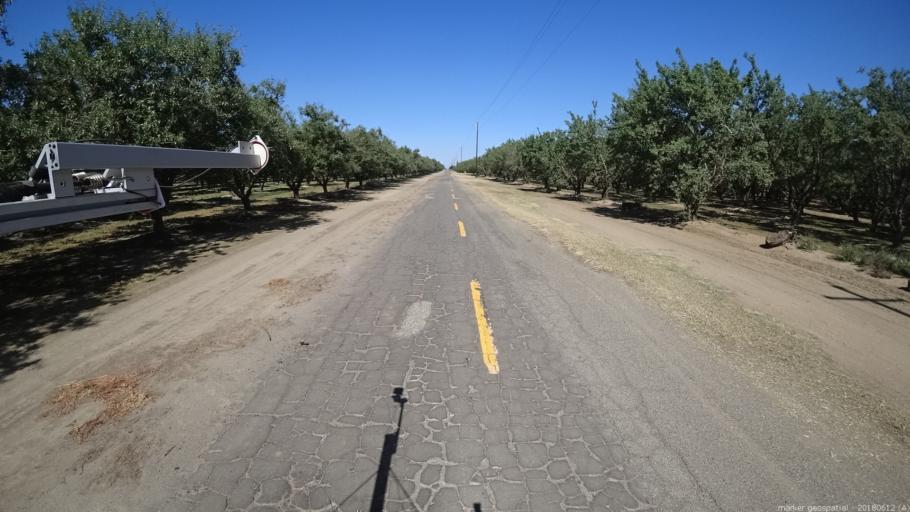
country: US
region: California
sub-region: Madera County
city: Chowchilla
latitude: 37.0325
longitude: -120.3947
